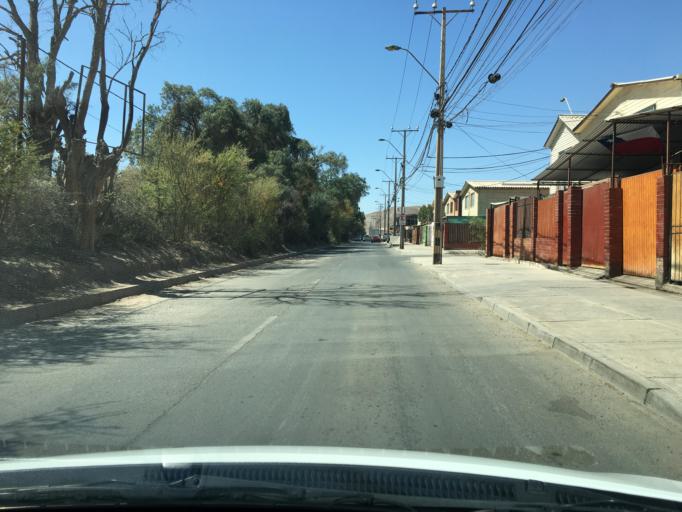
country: CL
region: Atacama
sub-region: Provincia de Copiapo
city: Copiapo
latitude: -27.4077
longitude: -70.2862
